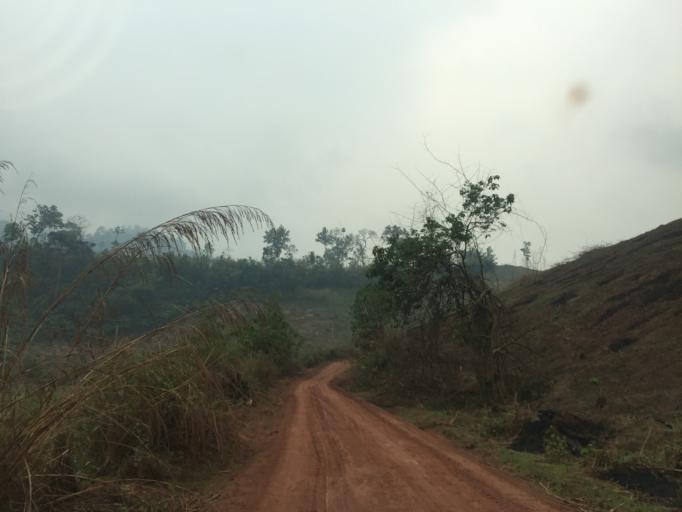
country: TH
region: Nan
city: Bo Kluea
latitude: 18.8473
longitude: 101.4174
